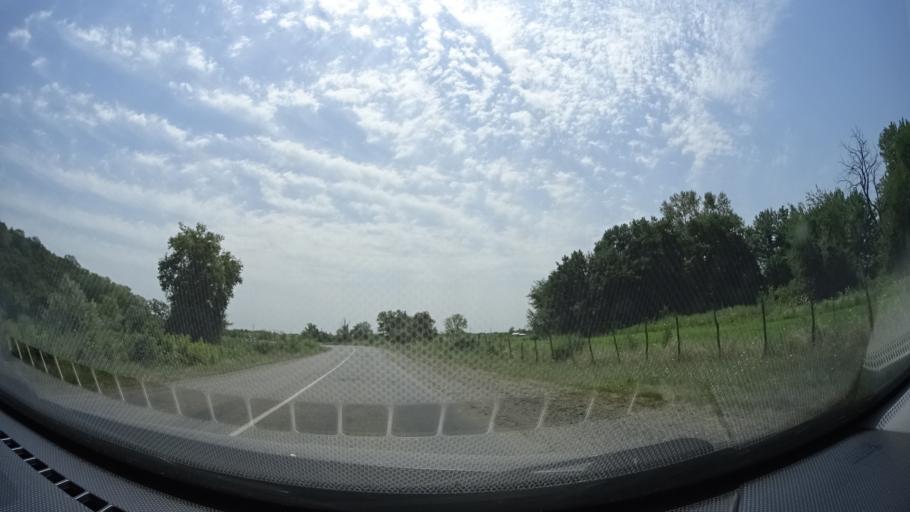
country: GE
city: Bagdadi
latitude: 41.8561
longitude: 46.0284
